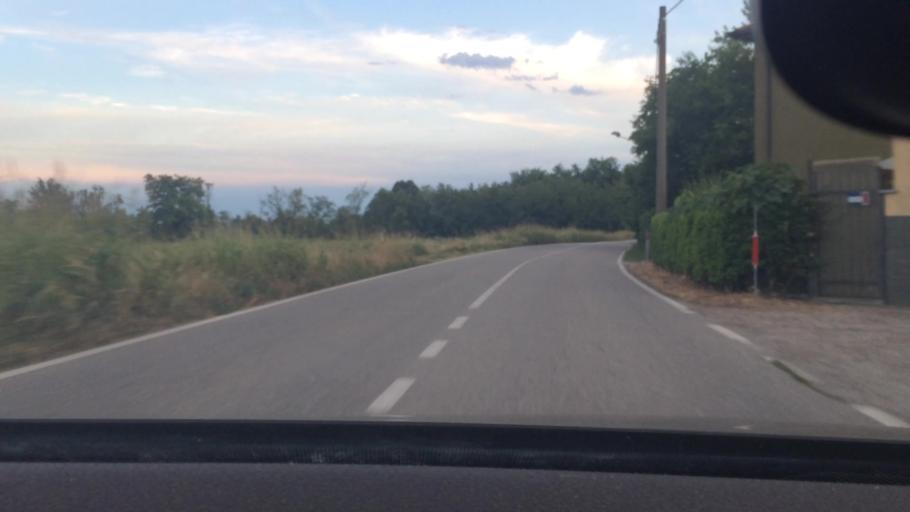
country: IT
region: Lombardy
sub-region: Citta metropolitana di Milano
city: Vanzago
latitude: 45.5211
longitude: 8.9865
